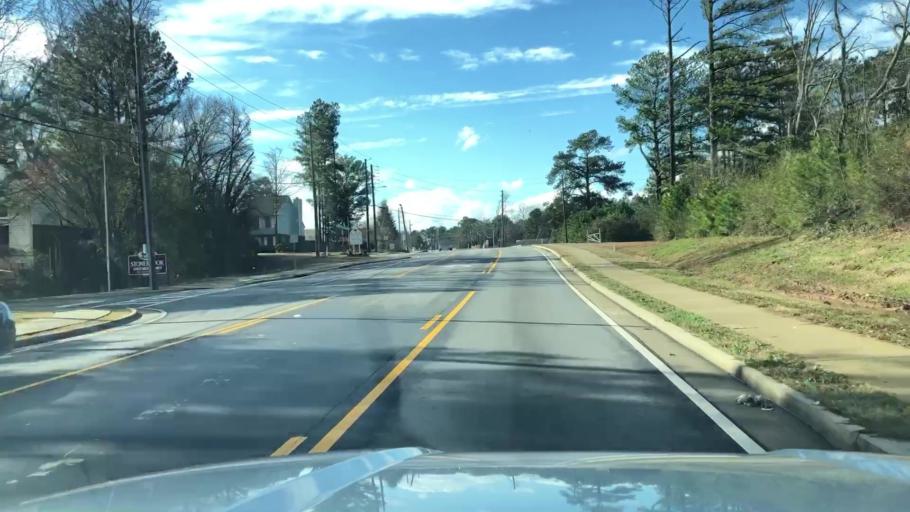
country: US
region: Georgia
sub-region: Fulton County
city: College Park
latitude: 33.6083
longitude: -84.4422
